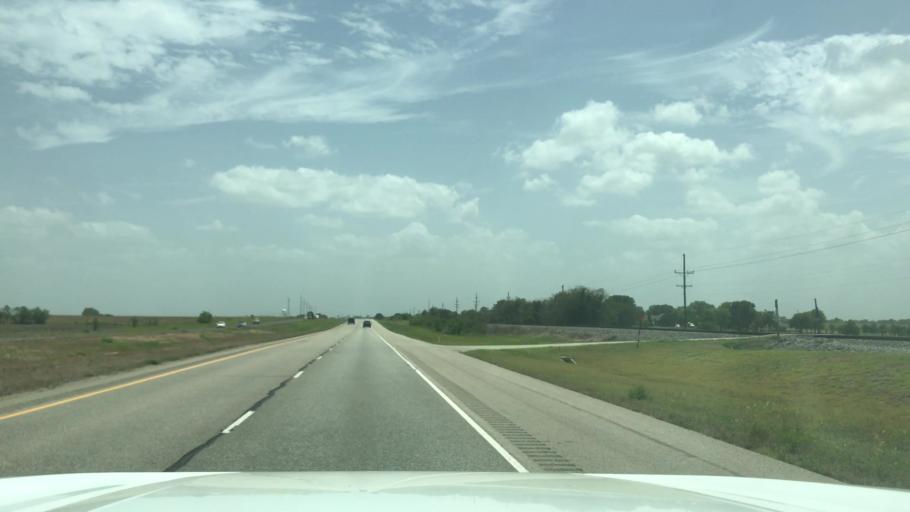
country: US
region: Texas
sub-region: Falls County
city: Marlin
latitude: 31.3454
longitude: -96.8943
